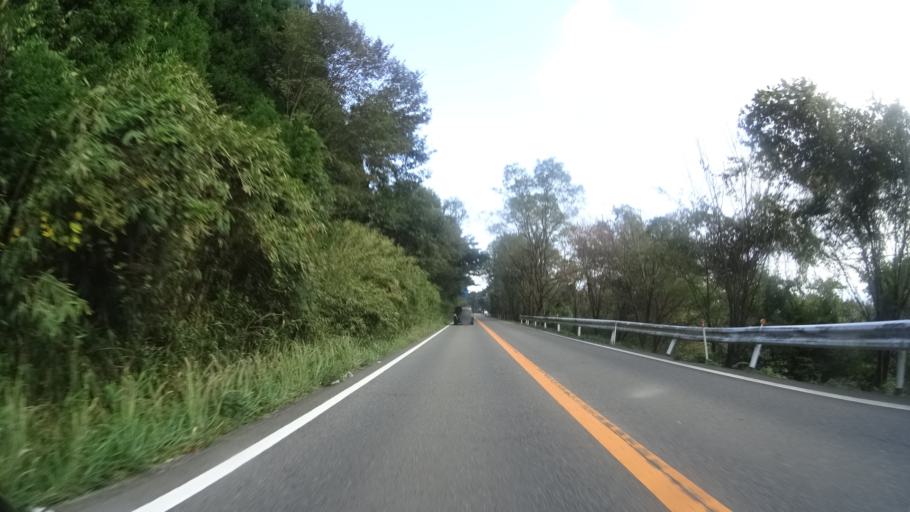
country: JP
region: Oita
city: Beppu
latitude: 33.2696
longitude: 131.4239
